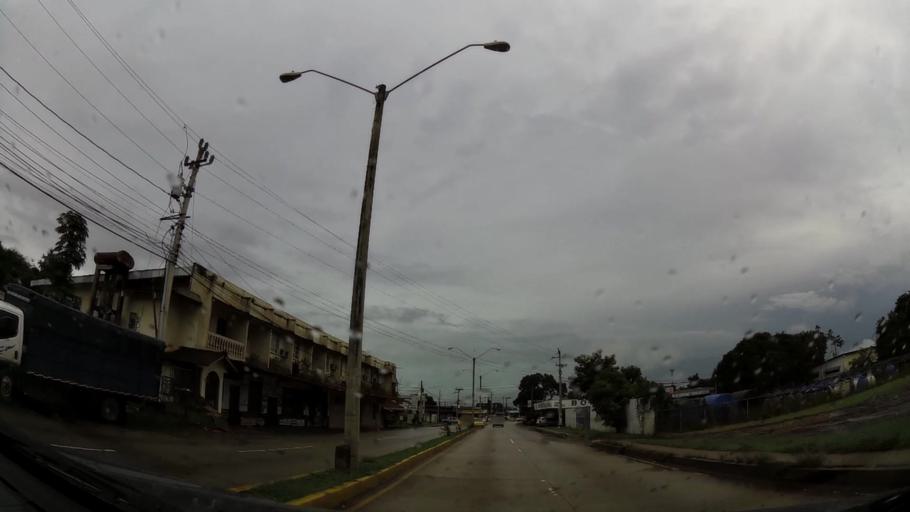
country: PA
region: Veraguas
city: Santiago de Veraguas
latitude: 8.0997
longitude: -80.9697
